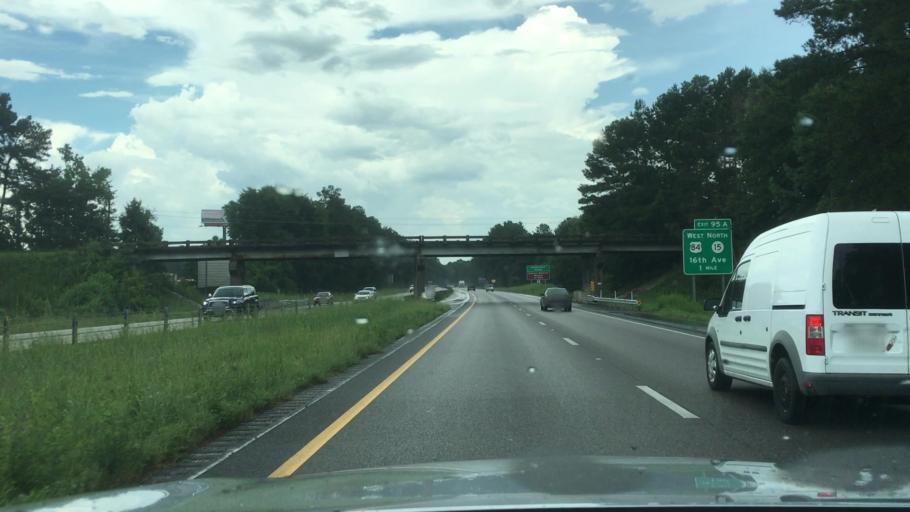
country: US
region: Mississippi
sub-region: Jones County
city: Laurel
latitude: 31.6701
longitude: -89.1578
